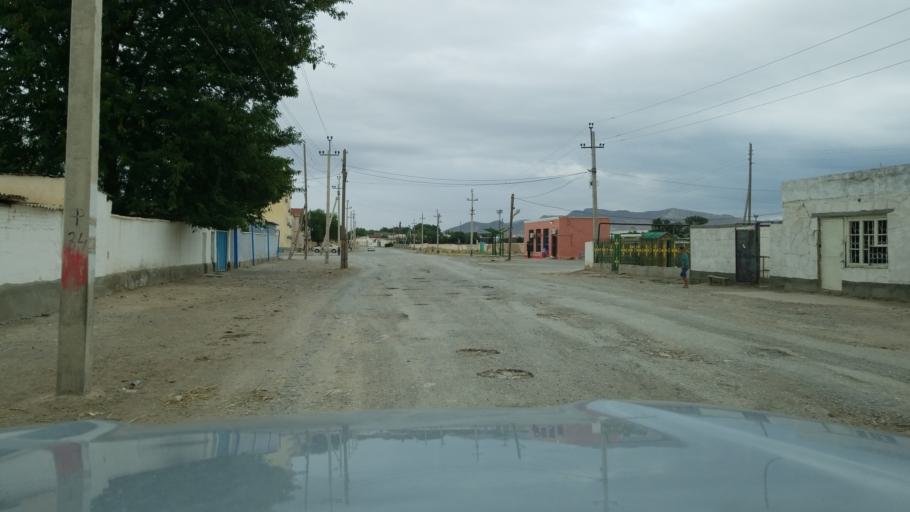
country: TM
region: Balkan
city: Serdar
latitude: 38.9820
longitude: 56.2657
